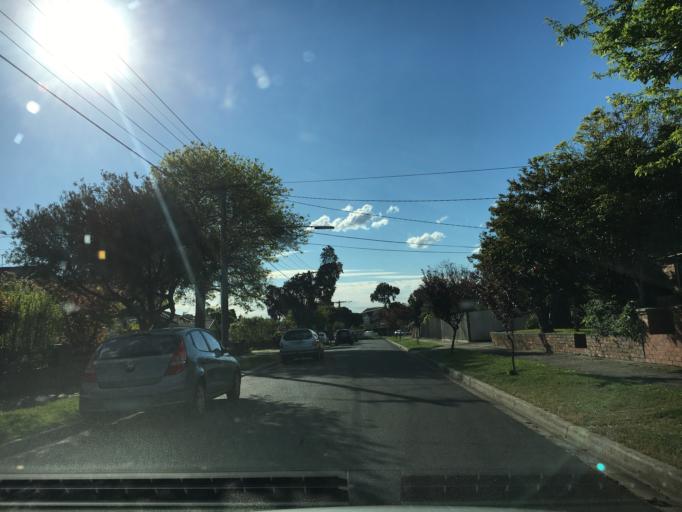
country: AU
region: Victoria
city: Clayton
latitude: -37.9010
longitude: 145.1083
